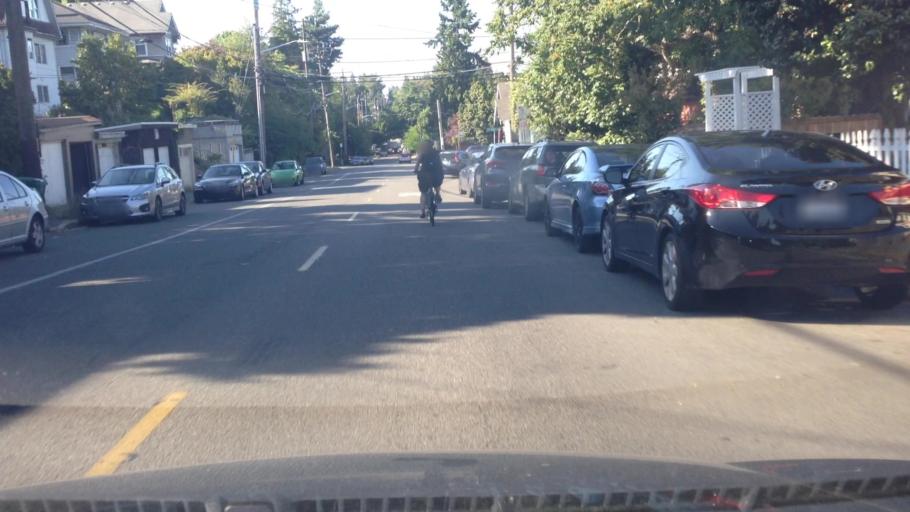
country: US
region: Washington
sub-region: King County
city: Seattle
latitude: 47.6674
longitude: -122.3065
